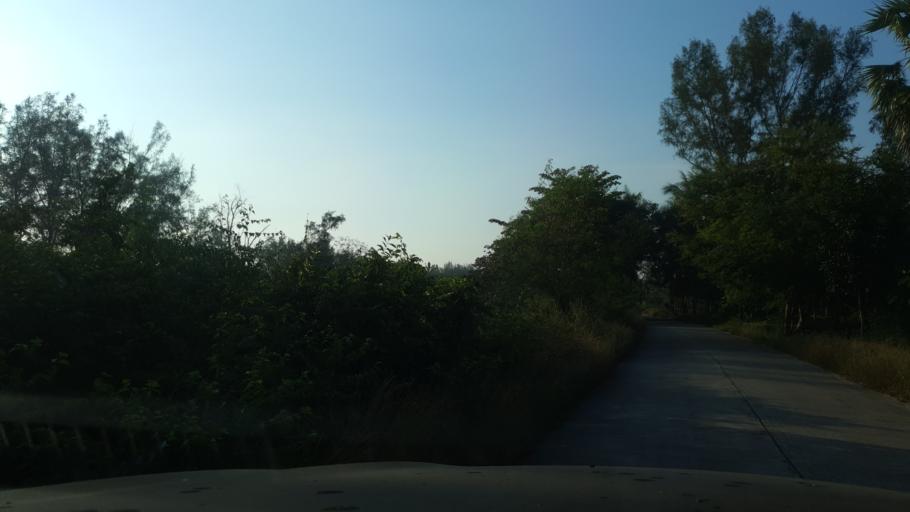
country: TH
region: Prachuap Khiri Khan
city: Bang Saphan
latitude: 11.2863
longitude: 99.5490
